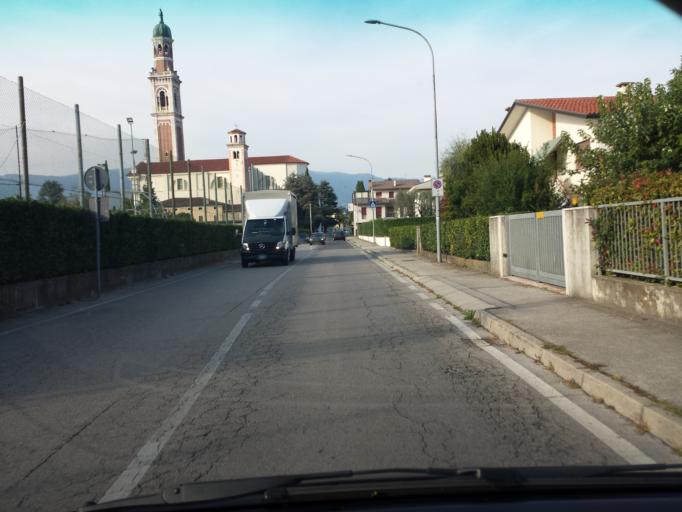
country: IT
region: Veneto
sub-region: Provincia di Vicenza
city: Nove
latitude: 45.7234
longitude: 11.6811
